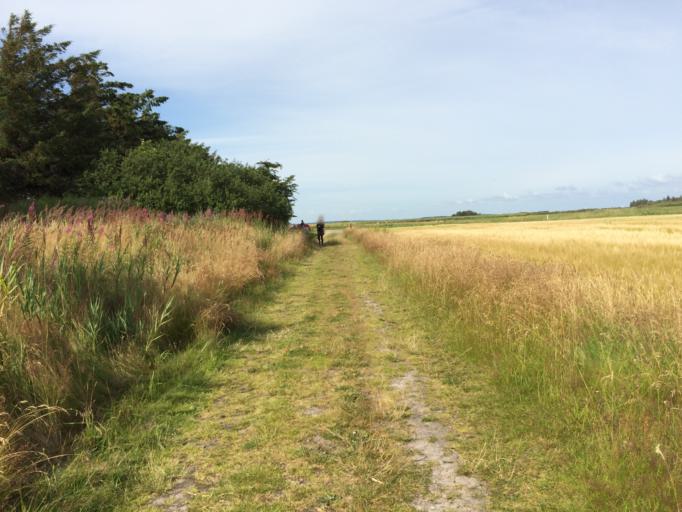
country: DK
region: Central Jutland
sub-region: Ringkobing-Skjern Kommune
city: Ringkobing
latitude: 56.1994
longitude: 8.1539
